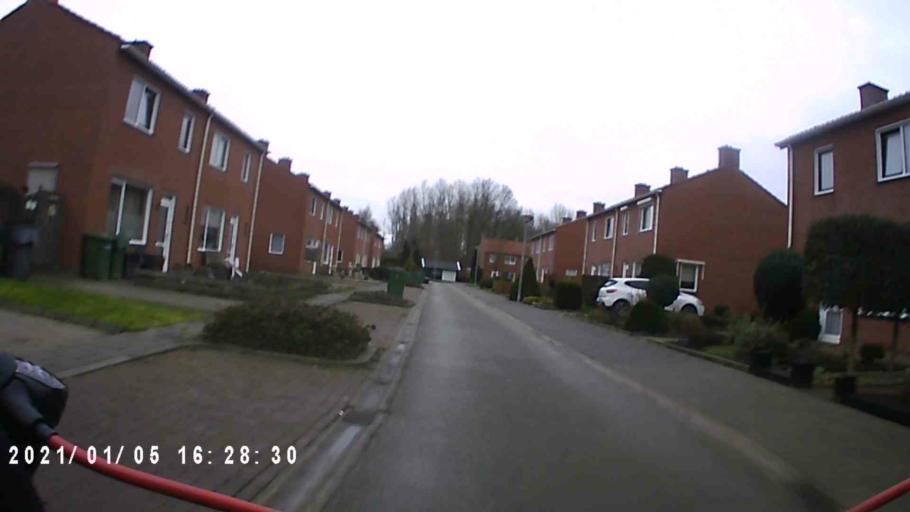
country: NL
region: Groningen
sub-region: Gemeente  Oldambt
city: Winschoten
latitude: 53.2049
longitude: 7.0400
